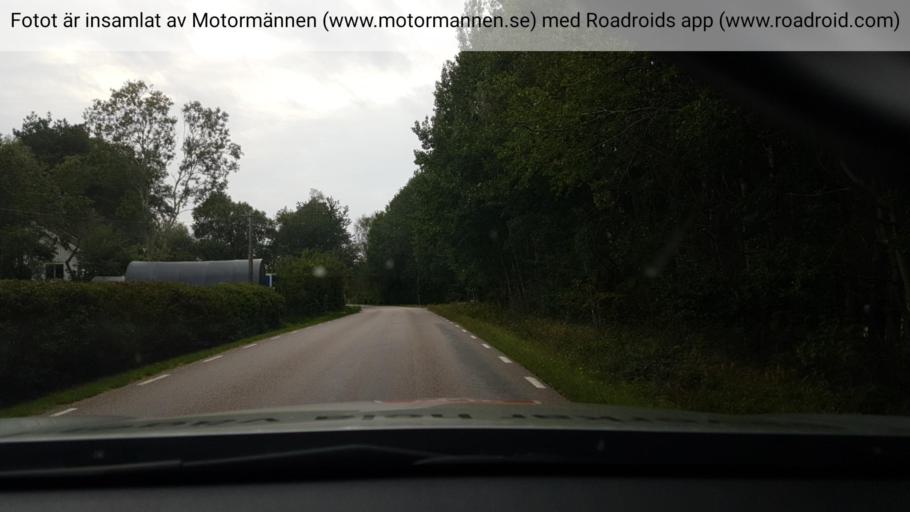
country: SE
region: Vaestra Goetaland
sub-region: Tanums Kommun
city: Grebbestad
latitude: 58.6338
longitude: 11.2847
